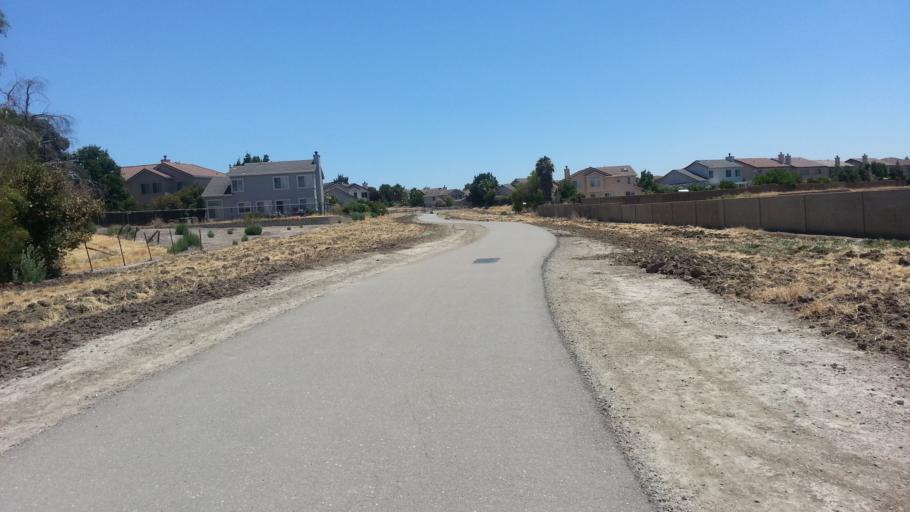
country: US
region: California
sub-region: Contra Costa County
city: Antioch
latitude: 37.9759
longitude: -121.7979
